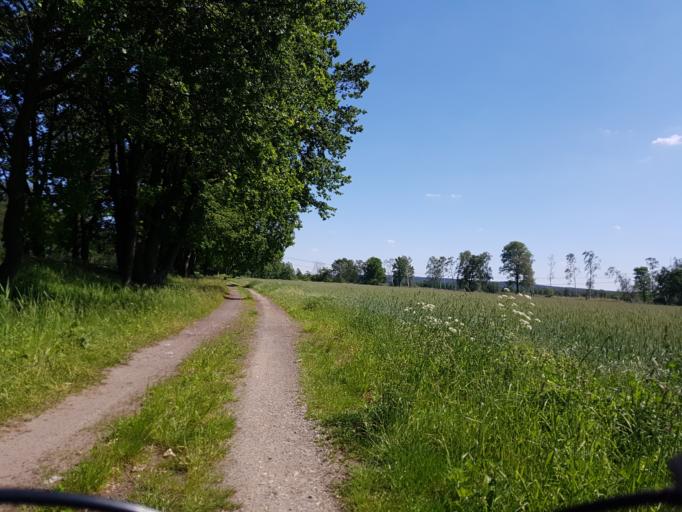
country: DE
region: Brandenburg
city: Elsterwerda
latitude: 51.4337
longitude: 13.5389
